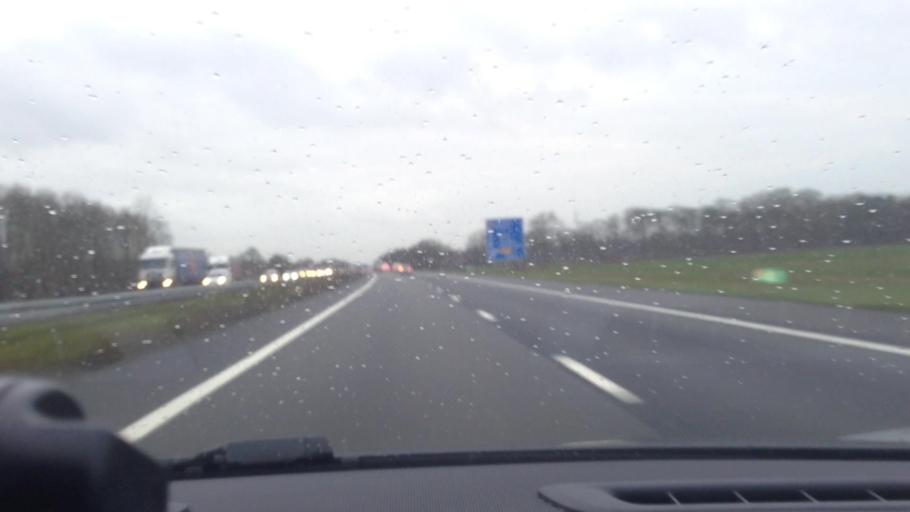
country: NL
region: Overijssel
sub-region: Gemeente Hof van Twente
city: Markelo
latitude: 52.2711
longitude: 6.4739
